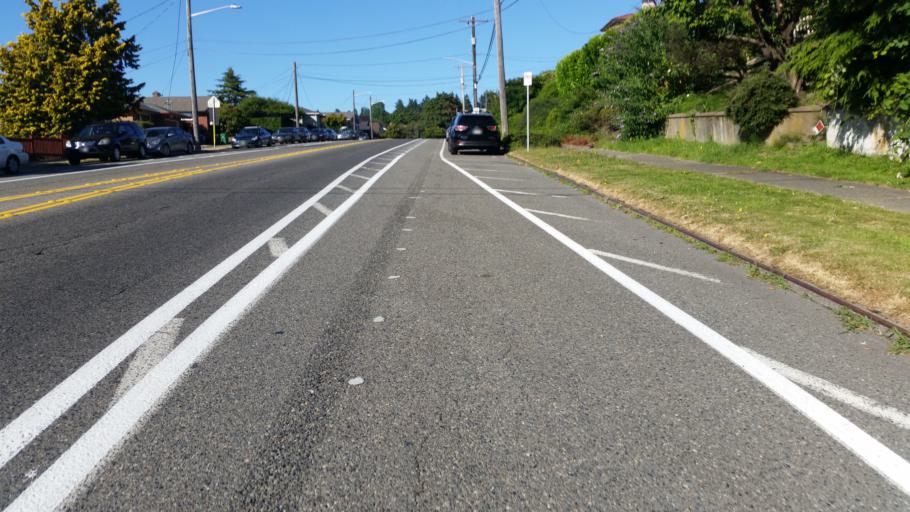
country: US
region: Washington
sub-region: King County
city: White Center
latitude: 47.5762
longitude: -122.4077
